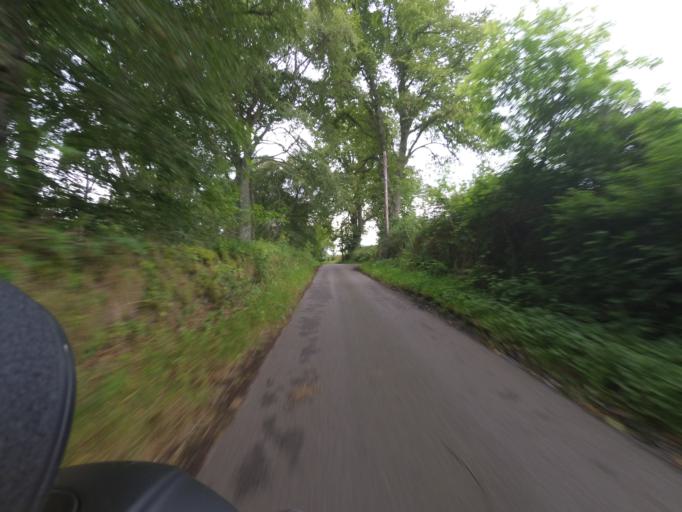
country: GB
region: Scotland
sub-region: Highland
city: Conon Bridge
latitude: 57.5138
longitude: -4.3724
